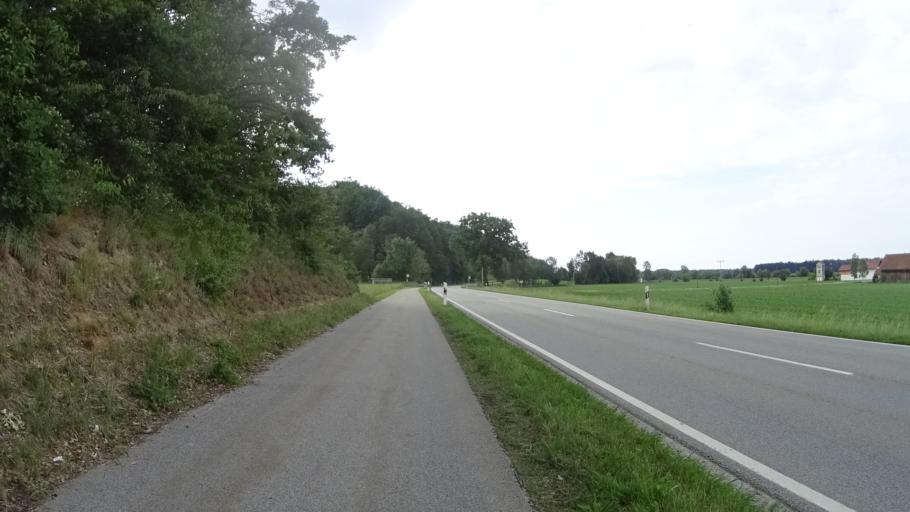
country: DE
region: Bavaria
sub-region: Lower Bavaria
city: Bogen
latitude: 48.8921
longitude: 12.7312
